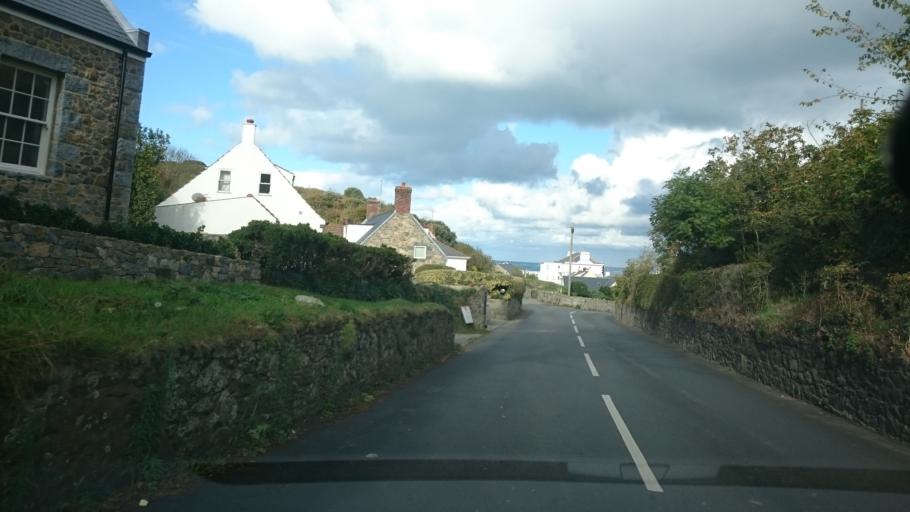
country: GG
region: St Peter Port
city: Saint Peter Port
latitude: 49.4324
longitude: -2.6588
